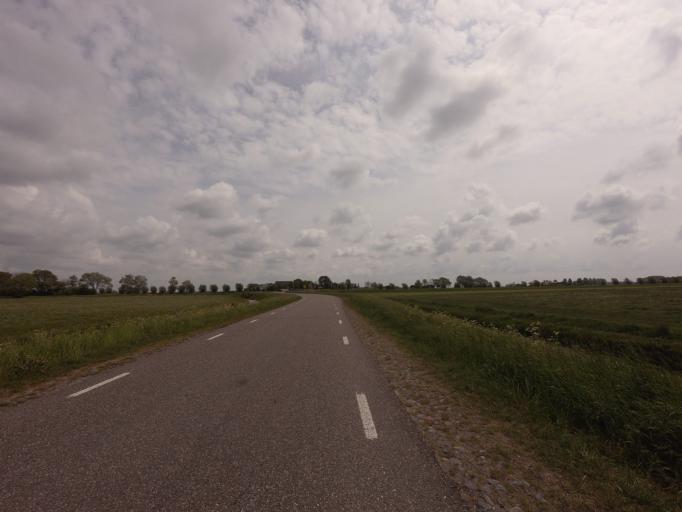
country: NL
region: Friesland
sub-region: Sudwest Fryslan
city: Bolsward
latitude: 53.0944
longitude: 5.5314
